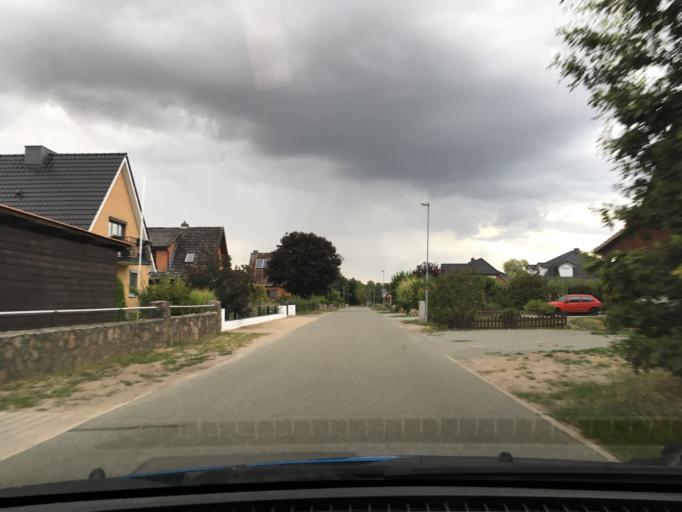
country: DE
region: Schleswig-Holstein
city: Lanze
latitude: 53.3901
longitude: 10.6072
